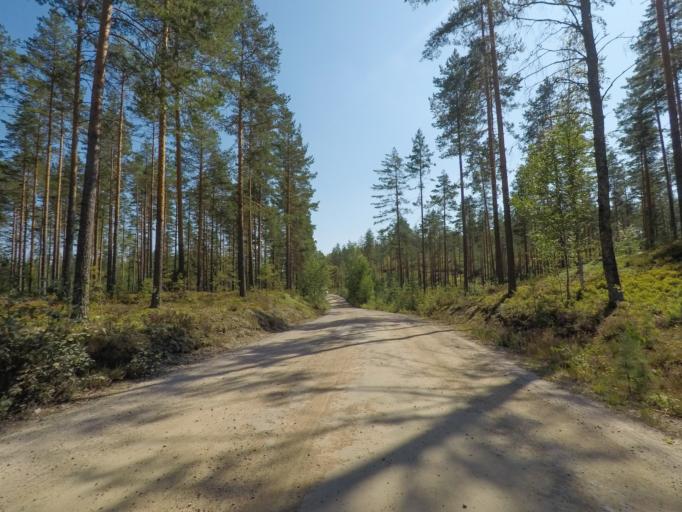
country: FI
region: Southern Savonia
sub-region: Mikkeli
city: Puumala
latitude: 61.4163
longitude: 28.0431
